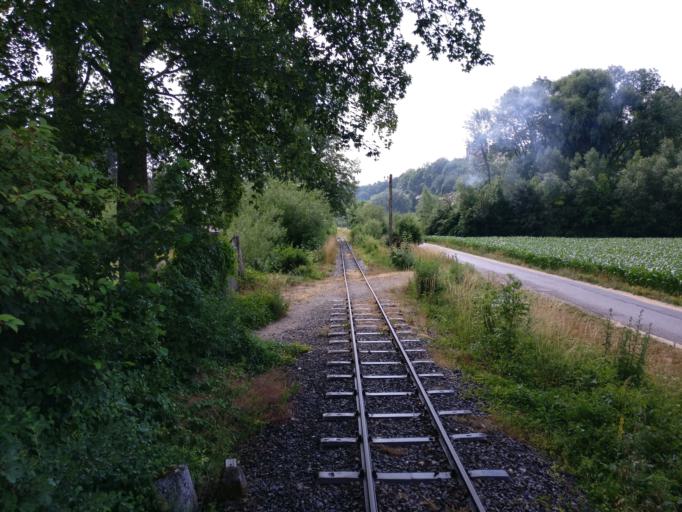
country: AT
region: Upper Austria
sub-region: Politischer Bezirk Steyr-Land
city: Garsten
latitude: 48.0413
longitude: 14.3833
